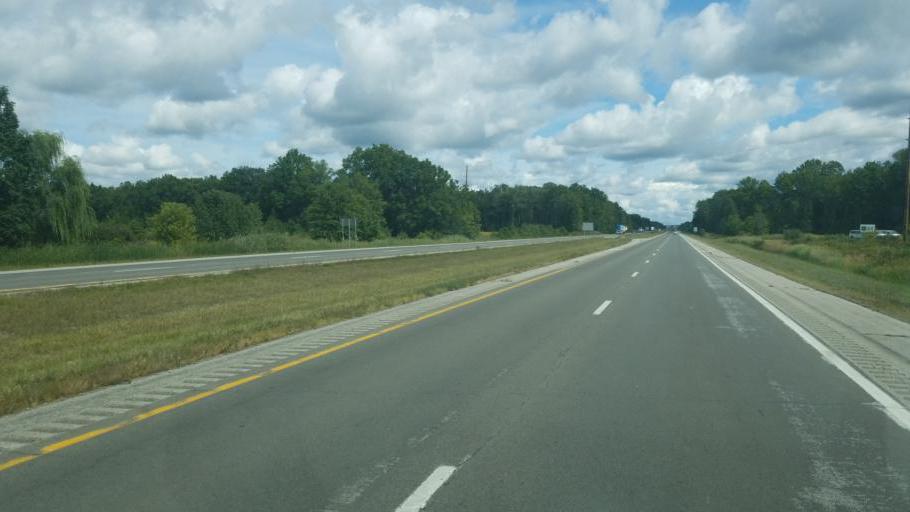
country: US
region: Ohio
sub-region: Lorain County
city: North Ridgeville
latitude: 41.3572
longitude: -82.0170
